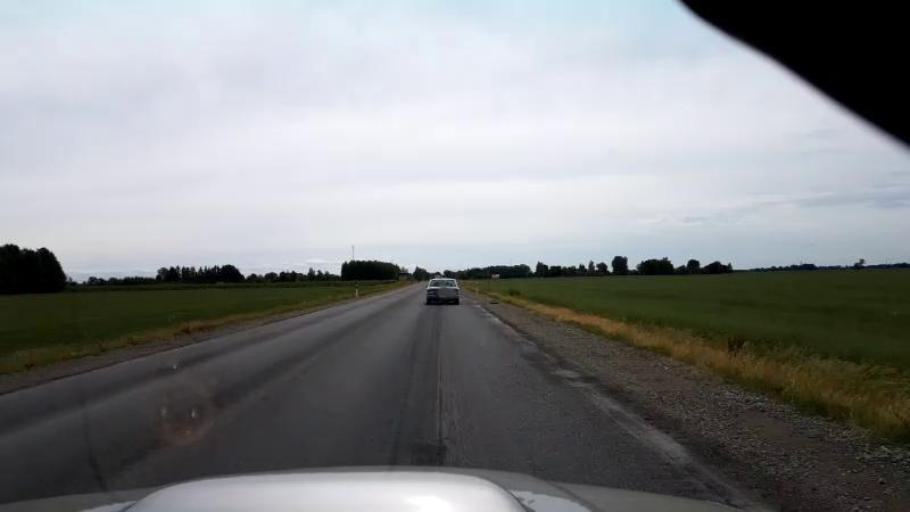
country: LV
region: Bauskas Rajons
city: Bauska
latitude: 56.3706
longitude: 24.2723
